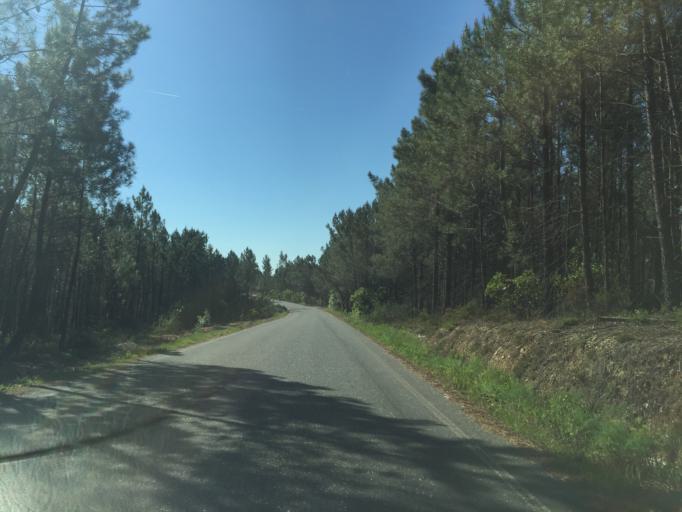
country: PT
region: Coimbra
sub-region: Pampilhosa da Serra
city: Pampilhosa da Serra
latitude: 40.0556
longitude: -7.8506
